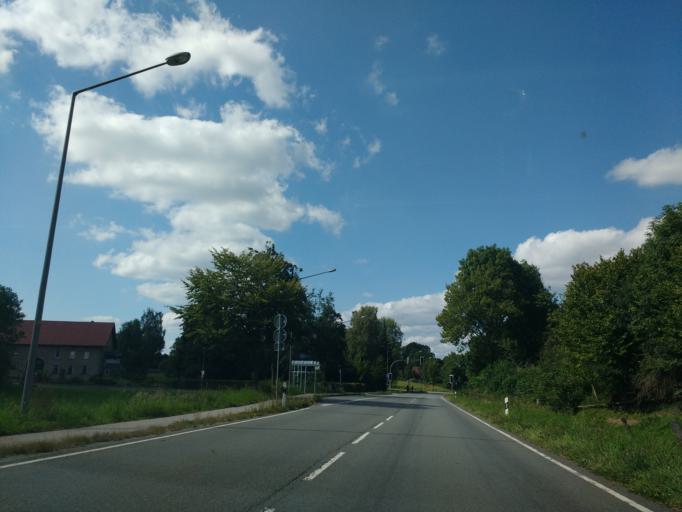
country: DE
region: North Rhine-Westphalia
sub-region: Regierungsbezirk Detmold
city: Lemgo
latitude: 51.9860
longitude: 8.8827
